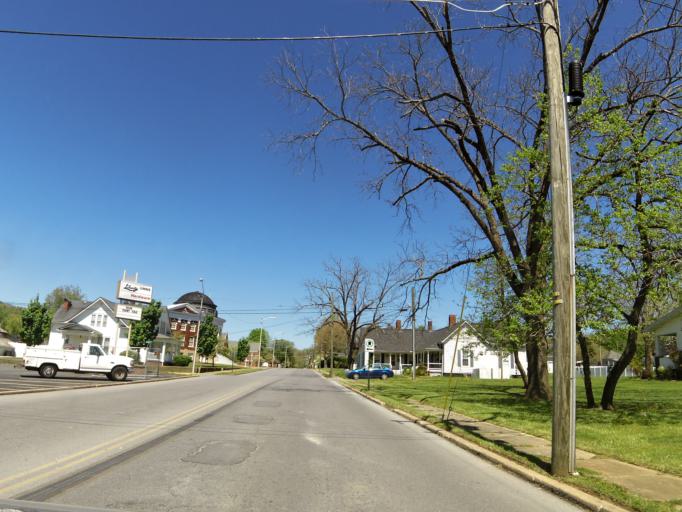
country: US
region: Tennessee
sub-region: Unicoi County
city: Erwin
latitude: 36.1438
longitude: -82.4156
